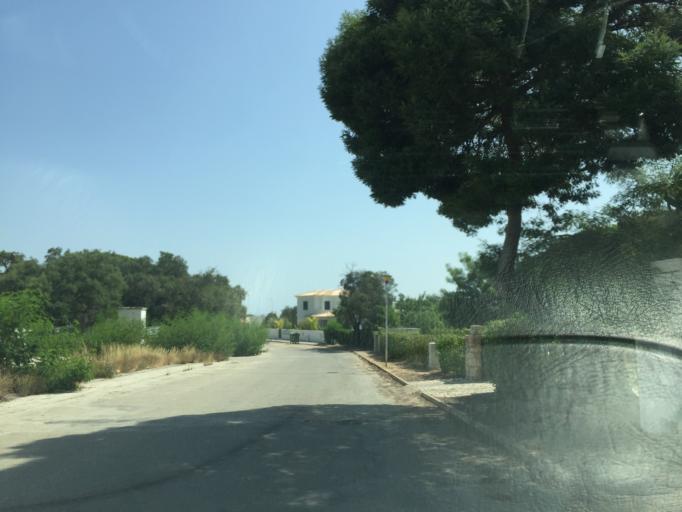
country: PT
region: Faro
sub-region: Albufeira
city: Ferreiras
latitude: 37.1068
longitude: -8.2048
